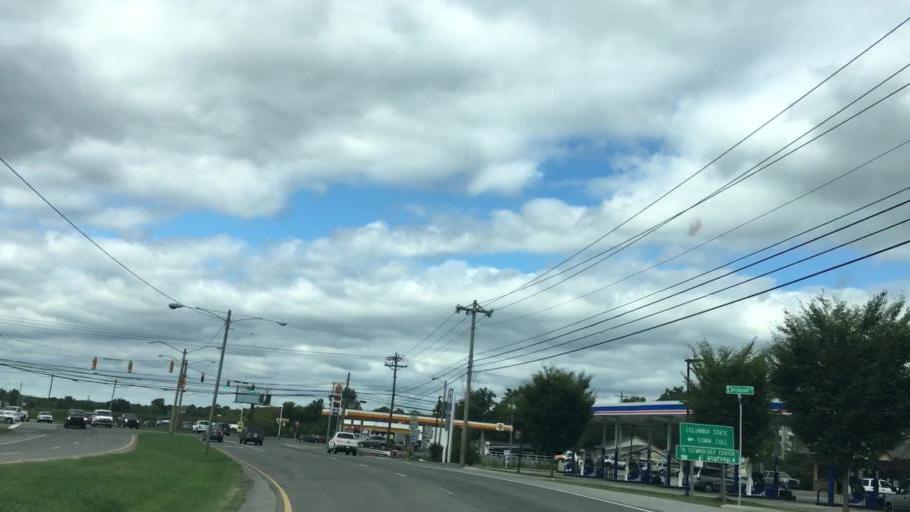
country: US
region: Tennessee
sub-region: Maury County
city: Columbia
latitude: 35.6166
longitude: -87.0648
